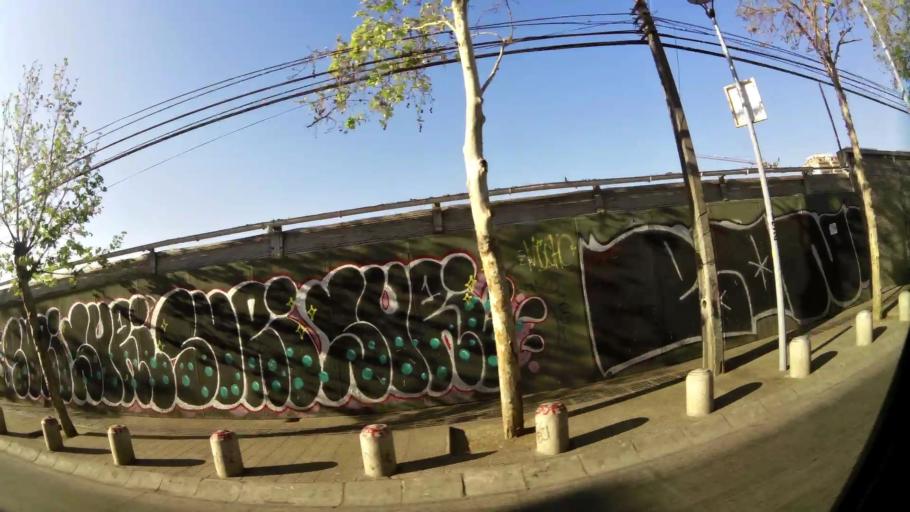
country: CL
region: Santiago Metropolitan
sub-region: Provincia de Santiago
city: Santiago
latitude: -33.4757
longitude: -70.6474
